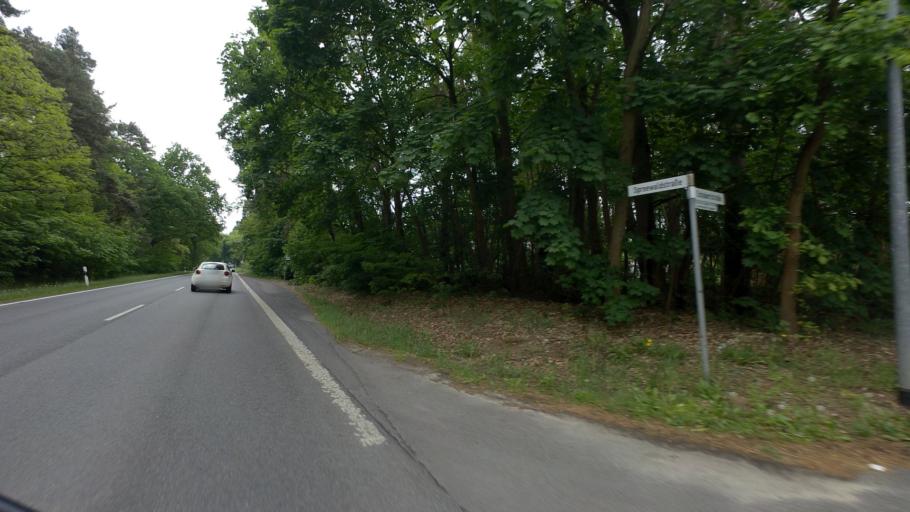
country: DE
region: Brandenburg
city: Bestensee
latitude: 52.2486
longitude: 13.6583
